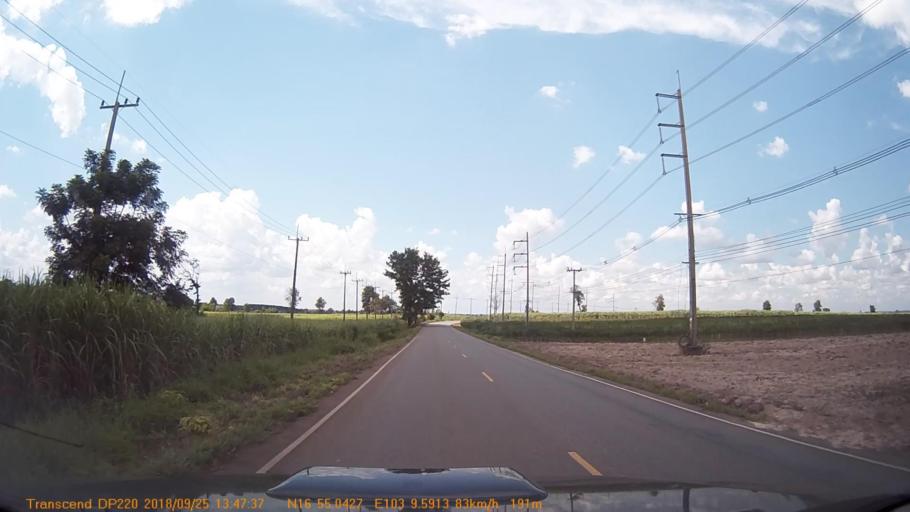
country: TH
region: Changwat Udon Thani
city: Si That
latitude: 16.9172
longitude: 103.1600
